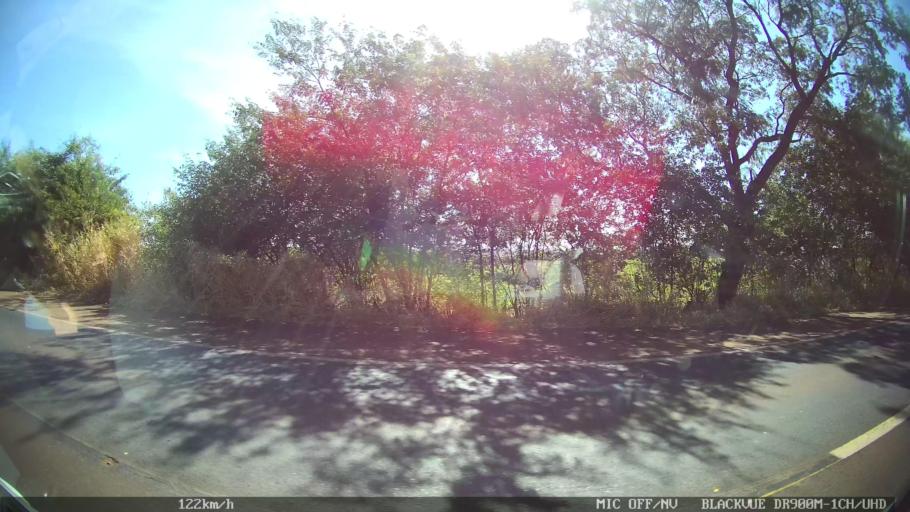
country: BR
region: Sao Paulo
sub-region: Barretos
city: Barretos
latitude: -20.5365
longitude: -48.6075
